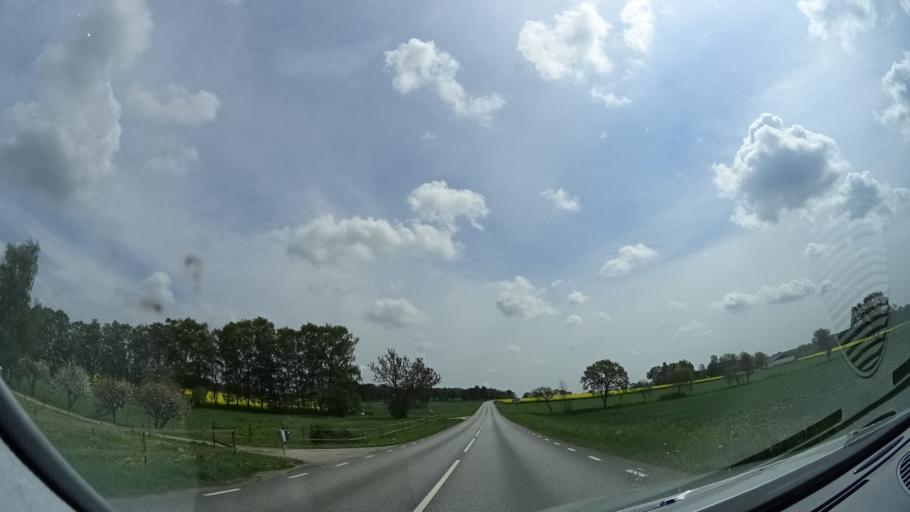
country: SE
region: Skane
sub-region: Hoors Kommun
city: Loberod
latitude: 55.7267
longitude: 13.4928
